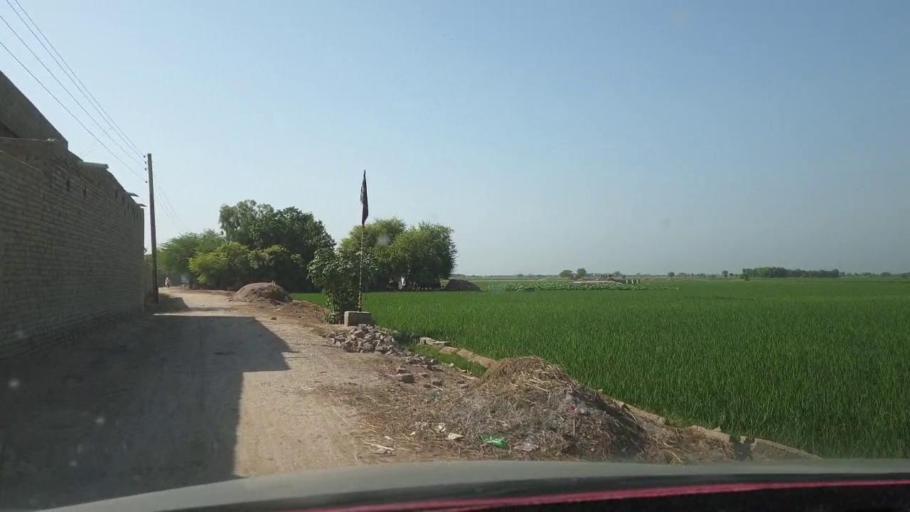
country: PK
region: Sindh
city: Nasirabad
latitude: 27.3826
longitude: 67.8795
